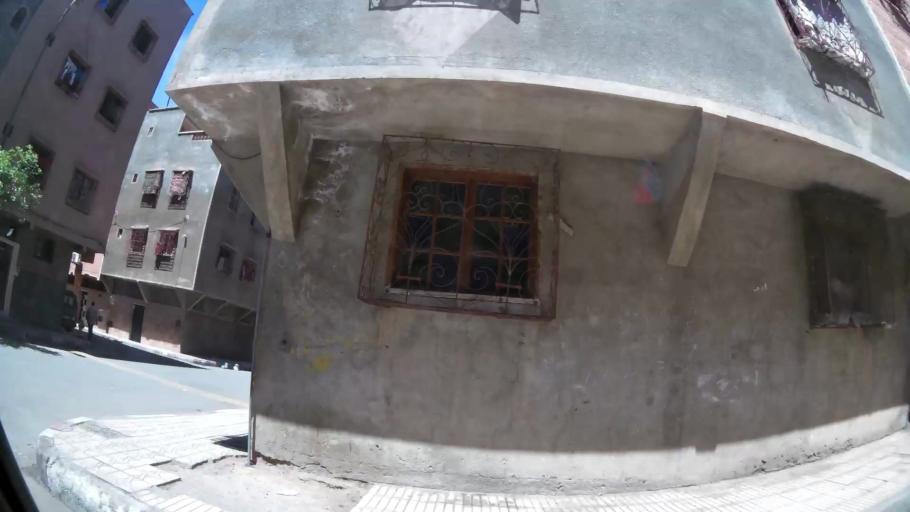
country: MA
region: Marrakech-Tensift-Al Haouz
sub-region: Marrakech
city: Marrakesh
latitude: 31.6575
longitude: -7.9925
